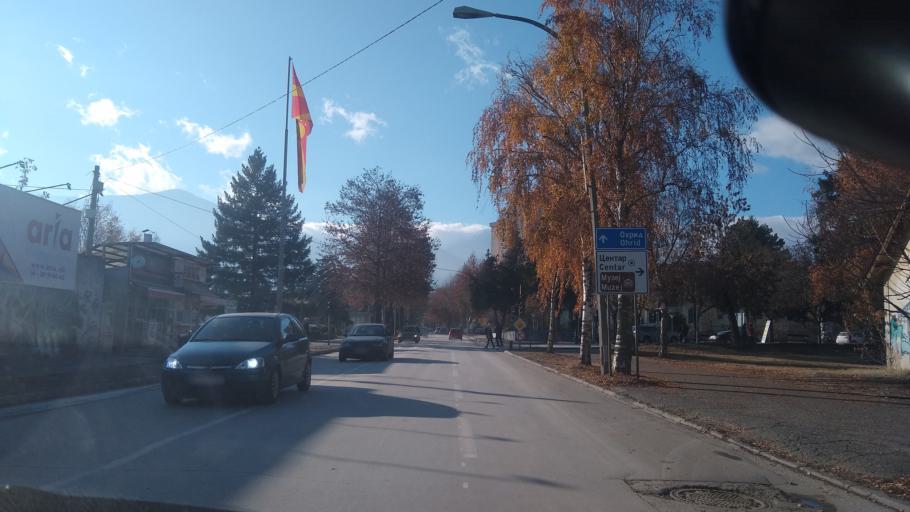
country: MK
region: Bitola
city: Bitola
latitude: 41.0234
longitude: 21.3377
